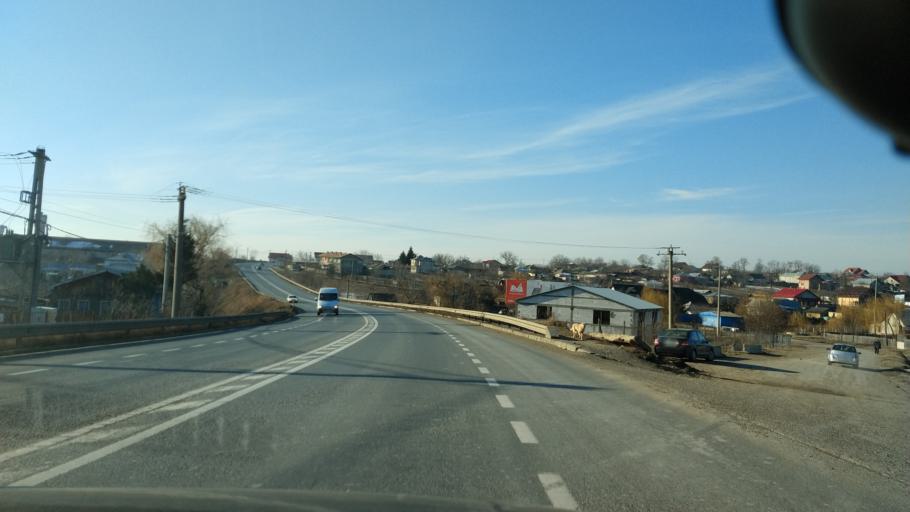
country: RO
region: Iasi
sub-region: Comuna Baltati
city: Baltati
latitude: 47.2200
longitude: 27.1228
